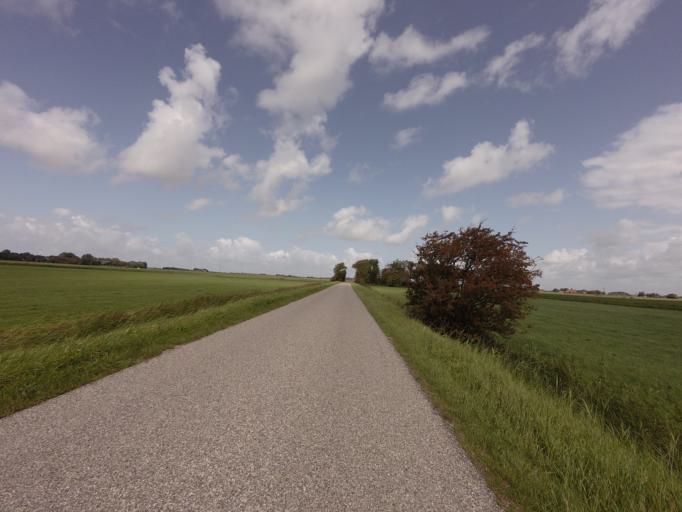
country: NL
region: Friesland
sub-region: Gemeente Franekeradeel
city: Sexbierum
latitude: 53.1593
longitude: 5.4830
